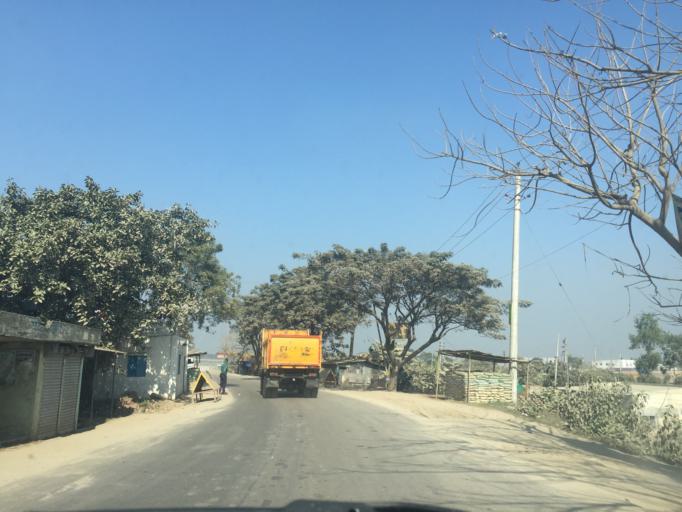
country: BD
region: Dhaka
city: Tungi
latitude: 23.8275
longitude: 90.3453
